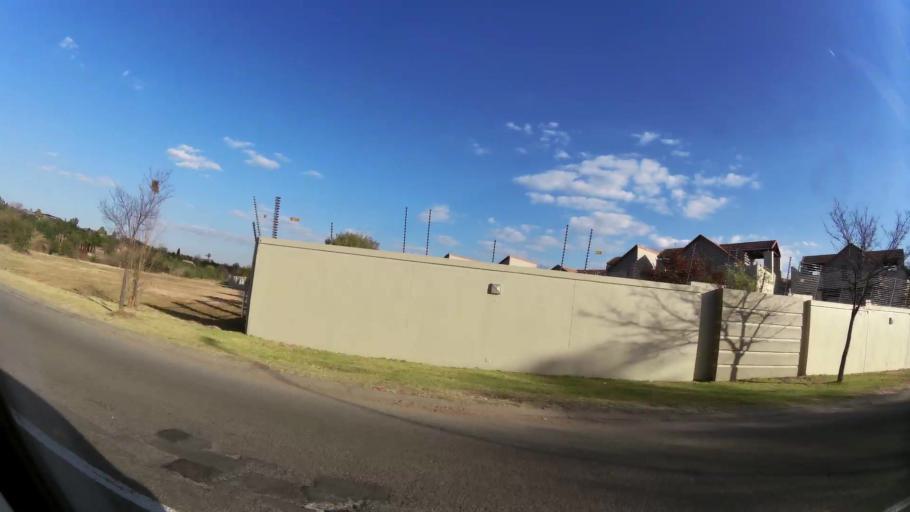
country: ZA
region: Gauteng
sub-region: City of Johannesburg Metropolitan Municipality
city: Diepsloot
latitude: -26.0107
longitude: 28.0062
